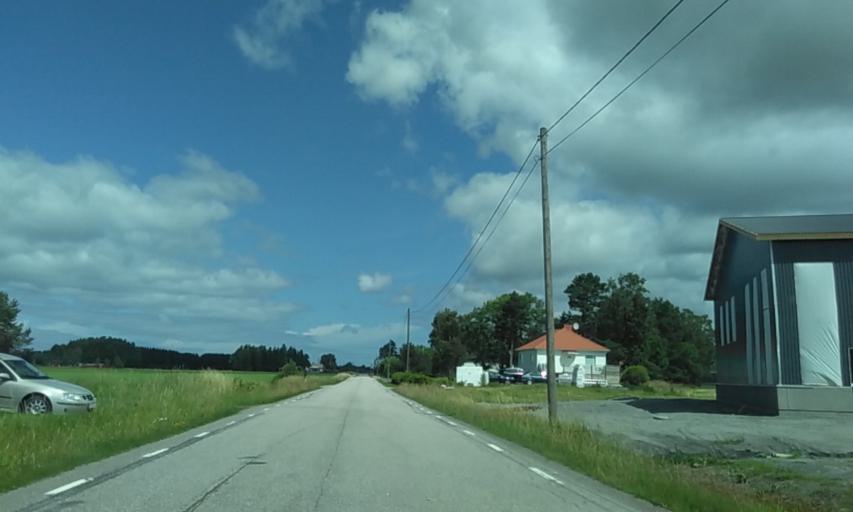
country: SE
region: Vaestra Goetaland
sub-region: Grastorps Kommun
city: Graestorp
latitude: 58.3644
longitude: 12.6825
